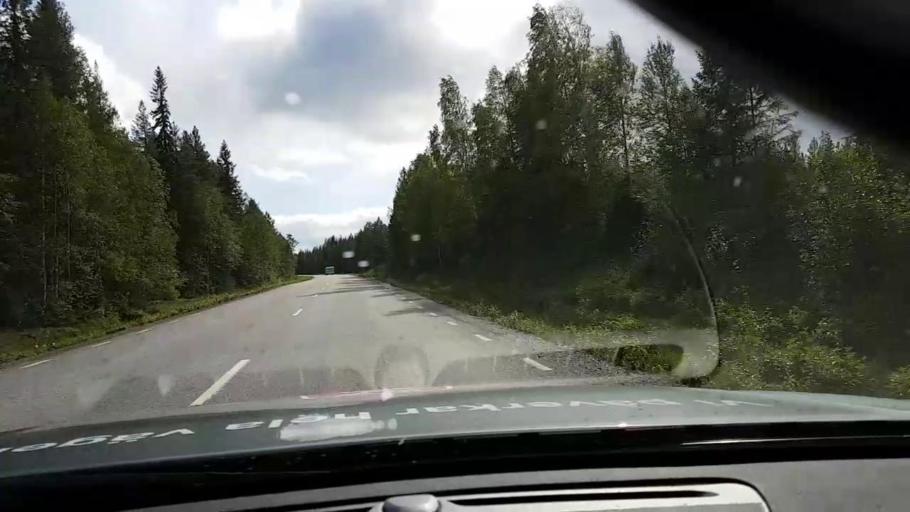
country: SE
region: Vaesternorrland
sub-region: OErnskoeldsviks Kommun
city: Bredbyn
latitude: 63.6265
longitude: 17.9089
